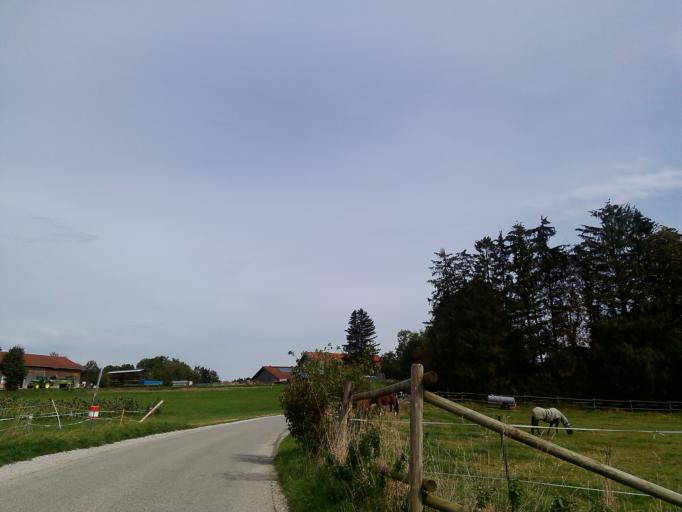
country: DE
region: Bavaria
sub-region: Upper Bavaria
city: Pocking
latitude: 47.9856
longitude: 11.2861
